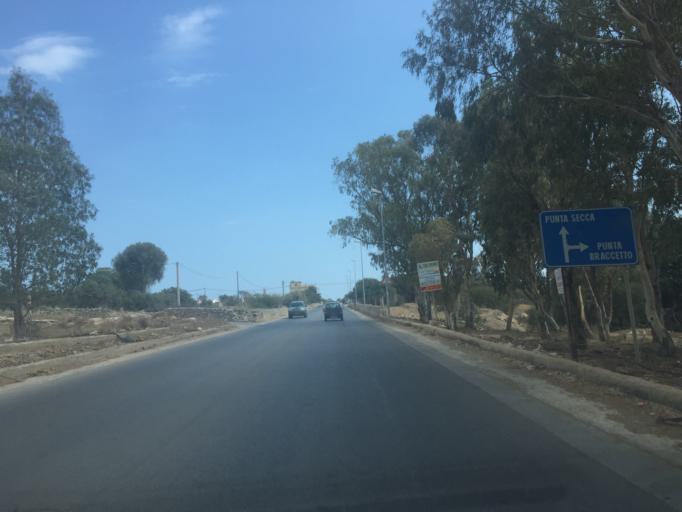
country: IT
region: Sicily
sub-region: Ragusa
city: Santa Croce Camerina
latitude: 36.8166
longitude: 14.5175
